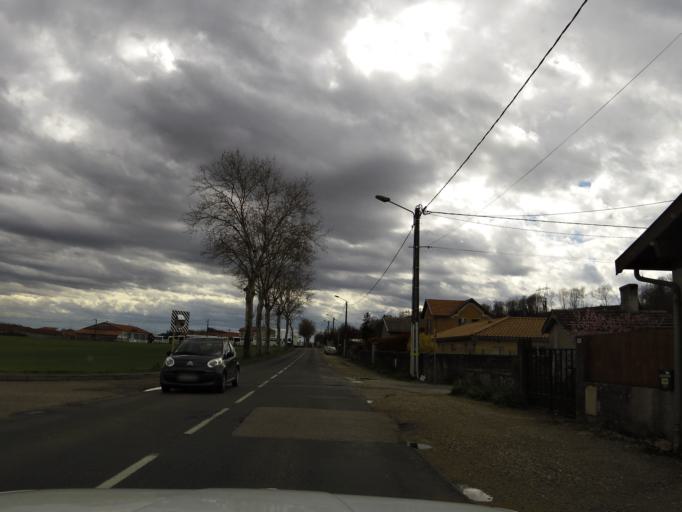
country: FR
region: Rhone-Alpes
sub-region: Departement de l'Ain
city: Meximieux
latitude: 45.9165
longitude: 5.2197
